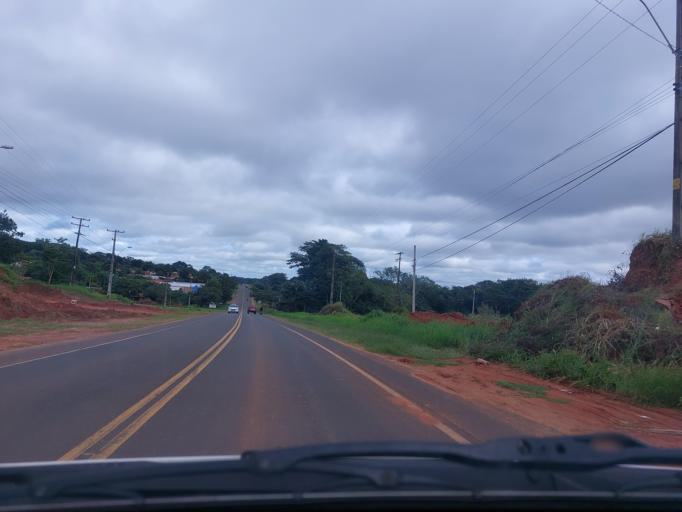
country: PY
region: San Pedro
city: Guayaybi
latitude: -24.6631
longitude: -56.4206
